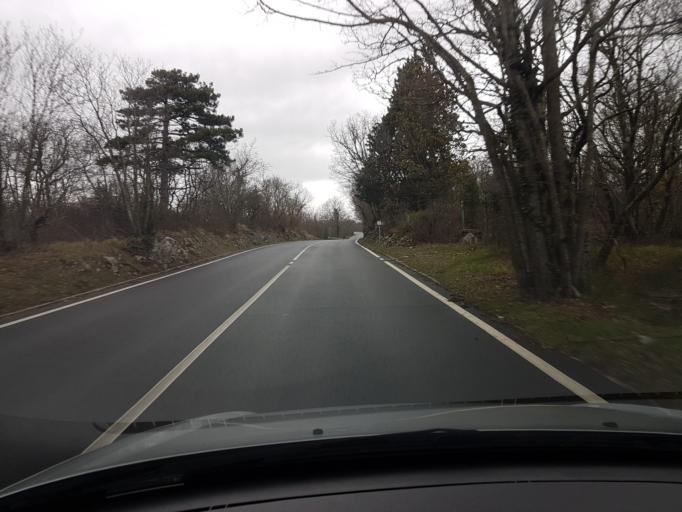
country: IT
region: Friuli Venezia Giulia
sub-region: Provincia di Trieste
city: Sgonico
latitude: 45.7339
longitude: 13.7273
